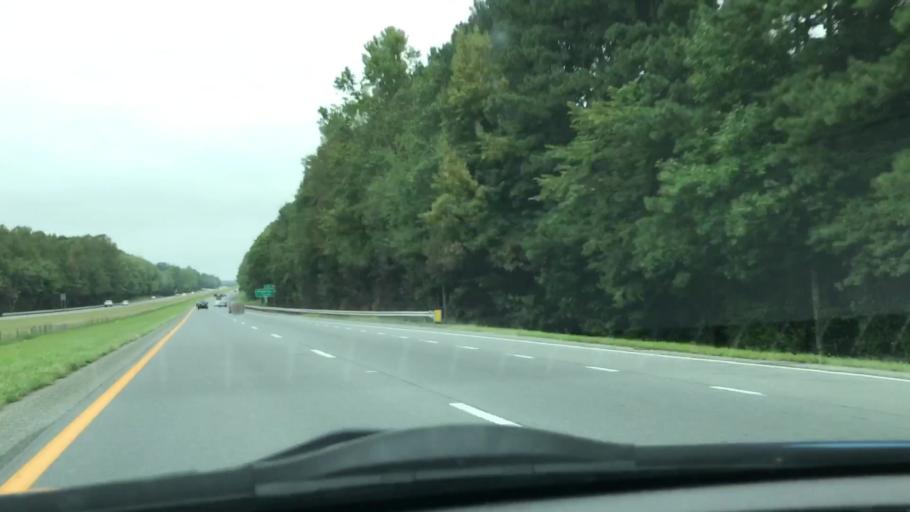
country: US
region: North Carolina
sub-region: Randolph County
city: Asheboro
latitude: 35.7579
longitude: -79.8264
